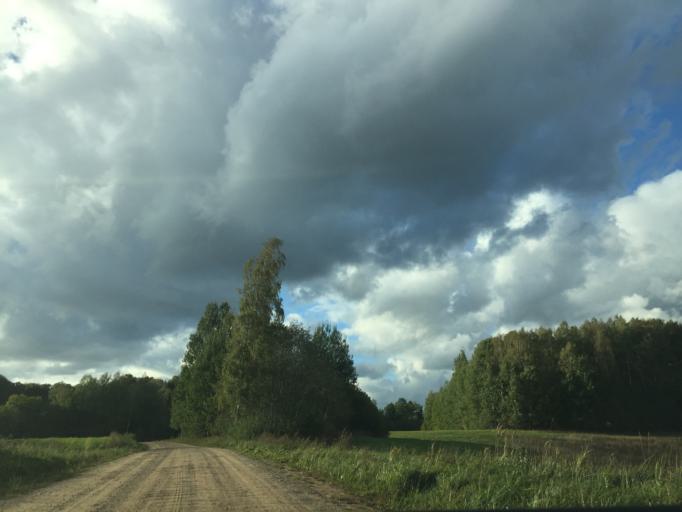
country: LV
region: Ligatne
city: Ligatne
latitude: 57.1374
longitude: 25.0871
